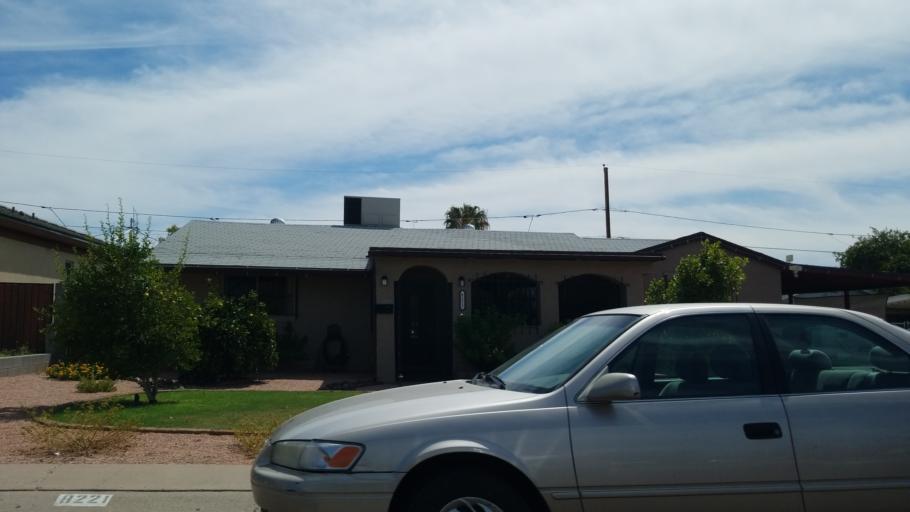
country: US
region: Arizona
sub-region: Maricopa County
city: Glendale
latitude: 33.5576
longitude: -112.1256
